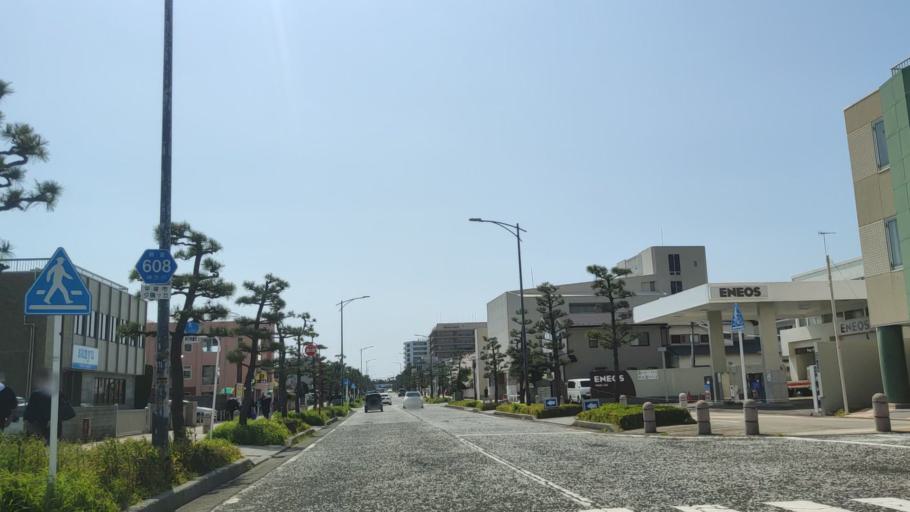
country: JP
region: Kanagawa
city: Hiratsuka
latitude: 35.3234
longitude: 139.3525
